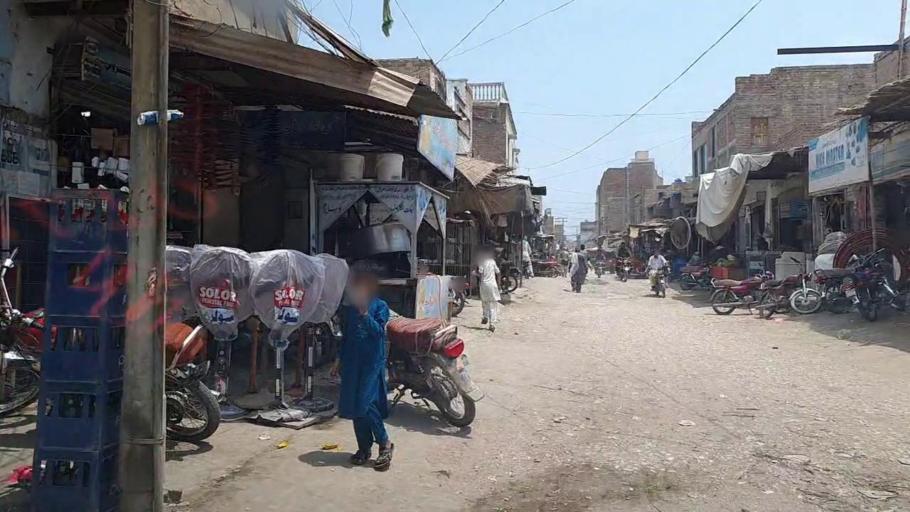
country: PK
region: Sindh
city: Khairpur
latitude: 28.0525
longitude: 69.6988
